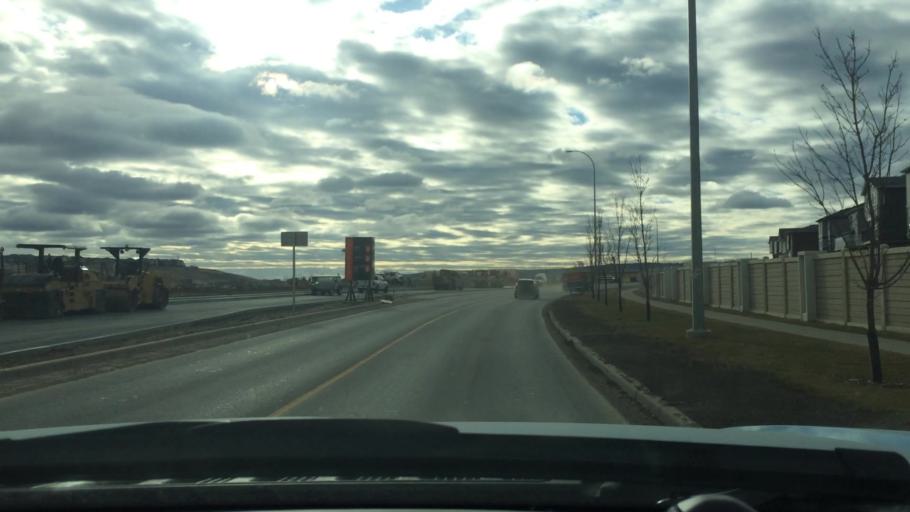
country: CA
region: Alberta
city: Calgary
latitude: 51.1798
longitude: -114.1337
